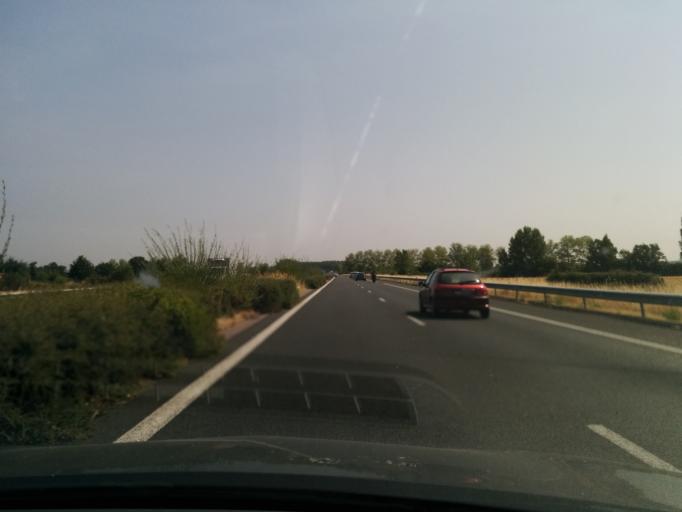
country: FR
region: Midi-Pyrenees
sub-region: Departement du Tarn
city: Marssac-sur-Tarn
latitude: 43.8937
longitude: 2.0256
